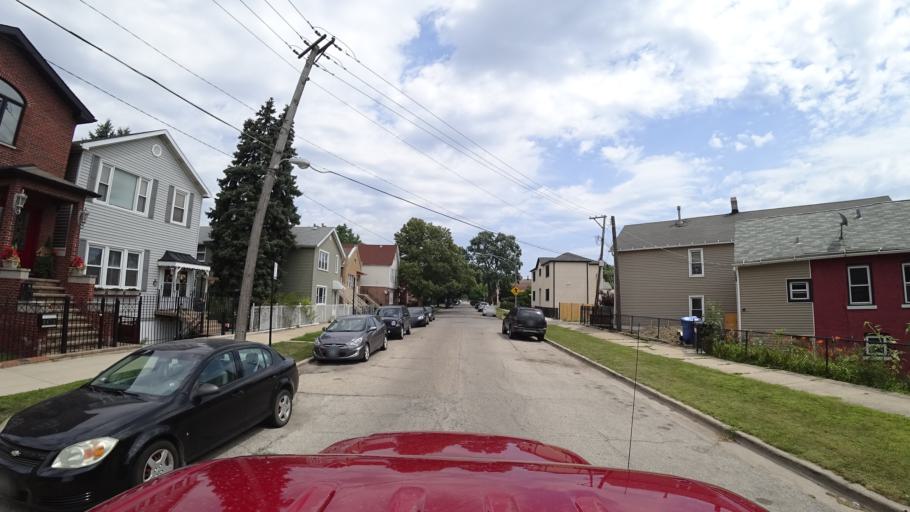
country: US
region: Illinois
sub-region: Cook County
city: Chicago
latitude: 41.8426
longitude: -87.6619
